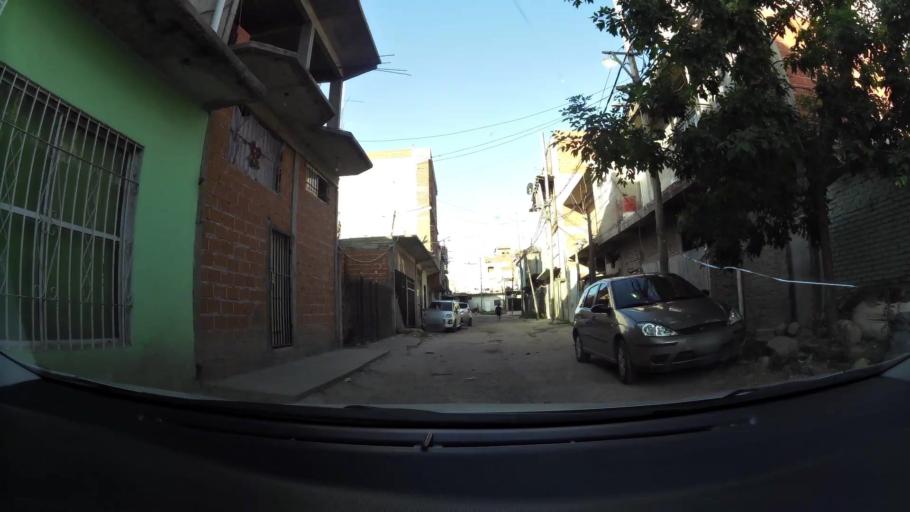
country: AR
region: Buenos Aires F.D.
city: Villa Lugano
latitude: -34.7080
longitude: -58.4834
